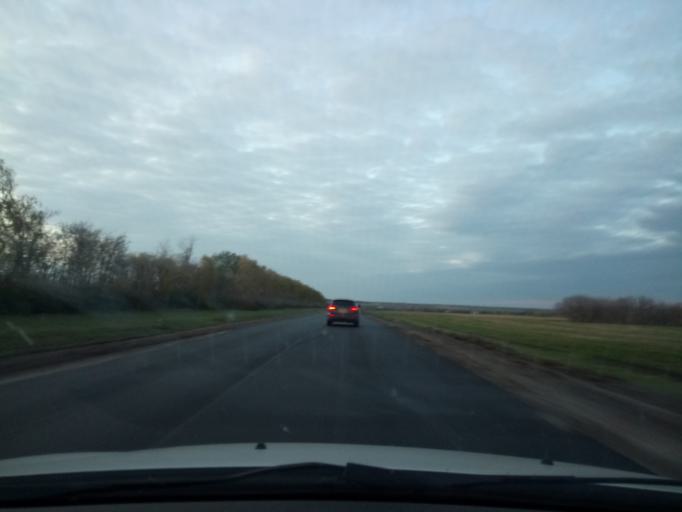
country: RU
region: Nizjnij Novgorod
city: Bol'shoye Murashkino
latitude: 55.8677
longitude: 44.7484
